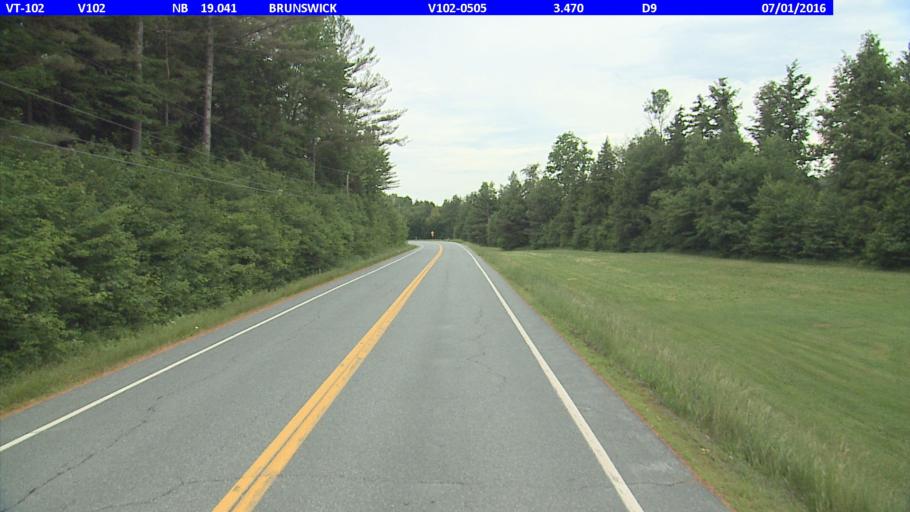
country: US
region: New Hampshire
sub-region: Coos County
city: Stratford
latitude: 44.7085
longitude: -71.6064
